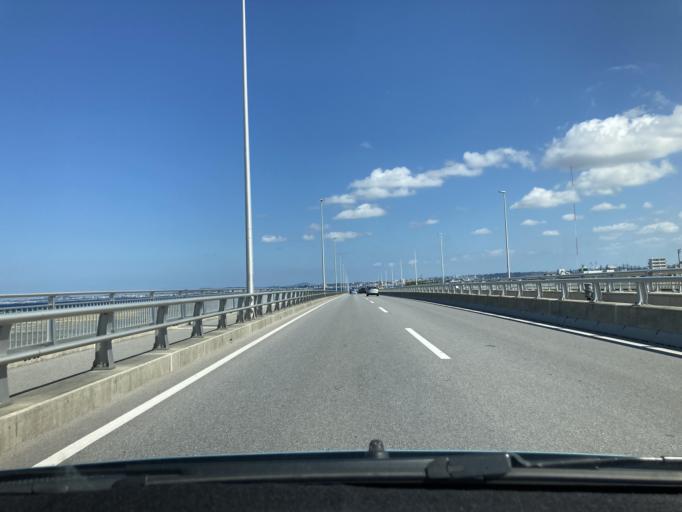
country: JP
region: Okinawa
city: Ginowan
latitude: 26.2682
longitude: 127.7030
